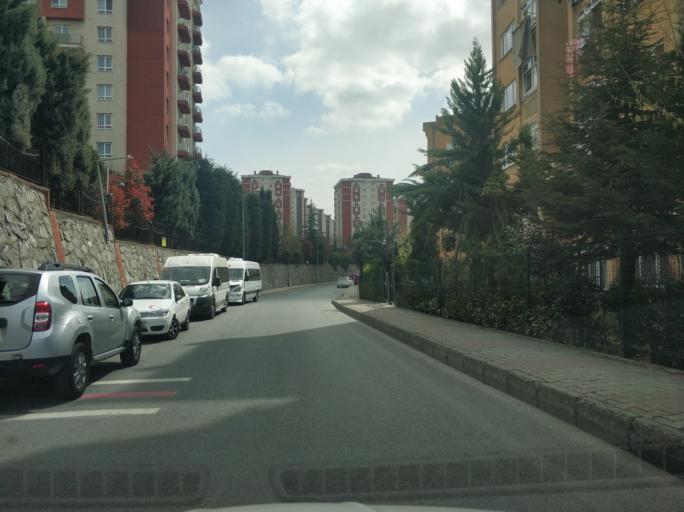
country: TR
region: Istanbul
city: Basaksehir
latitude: 41.0950
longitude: 28.8035
